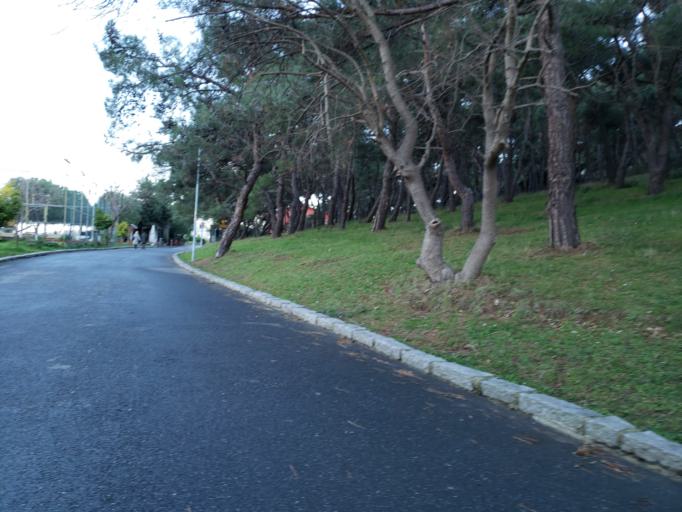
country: TR
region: Istanbul
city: Adalan
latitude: 40.8840
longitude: 29.0973
